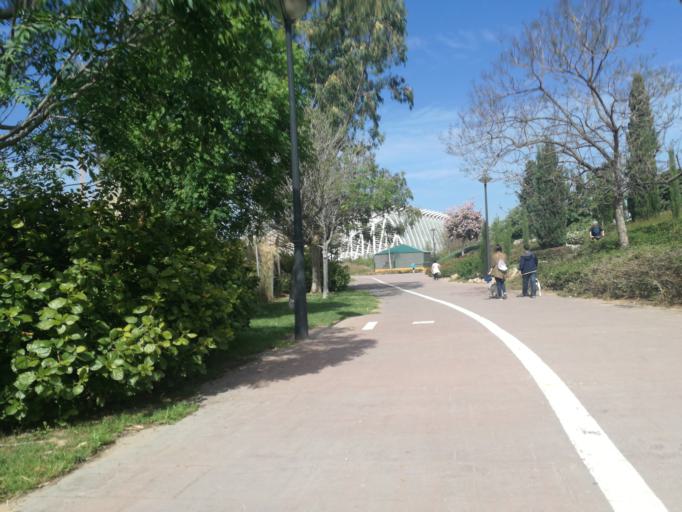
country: ES
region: Valencia
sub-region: Provincia de Valencia
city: Valencia
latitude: 39.4544
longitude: -0.3456
